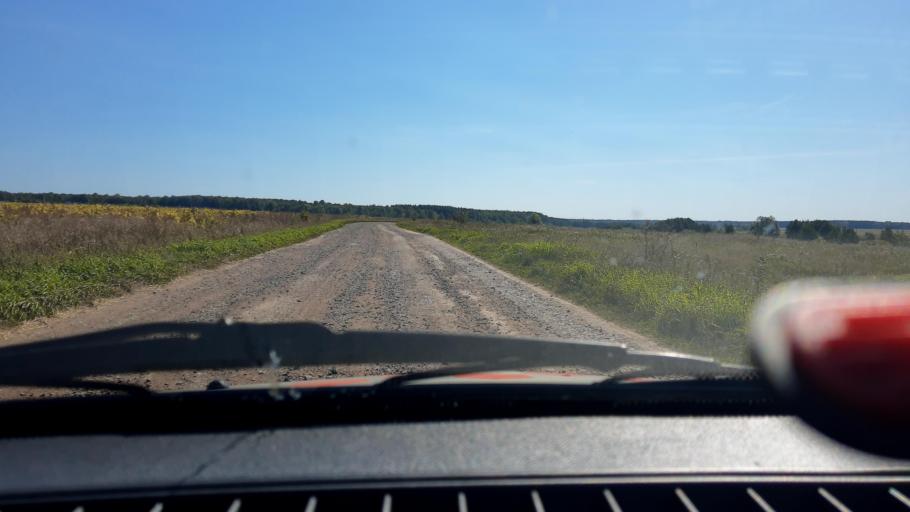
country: RU
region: Bashkortostan
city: Asanovo
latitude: 54.8112
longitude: 55.5835
